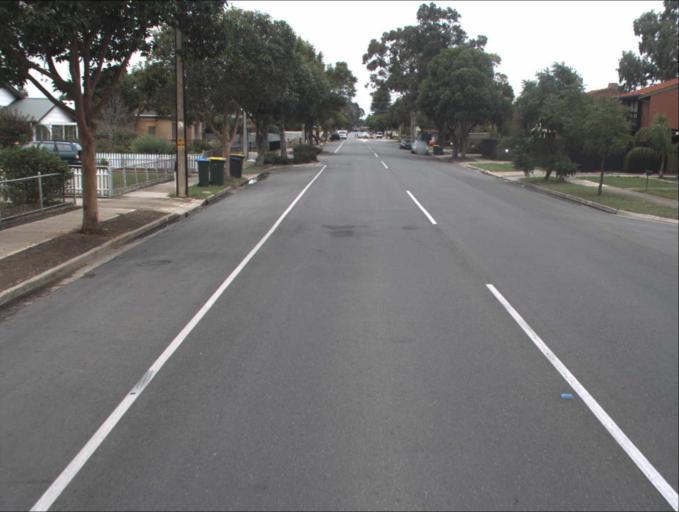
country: AU
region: South Australia
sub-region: Prospect
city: Prospect
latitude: -34.8869
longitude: 138.5760
